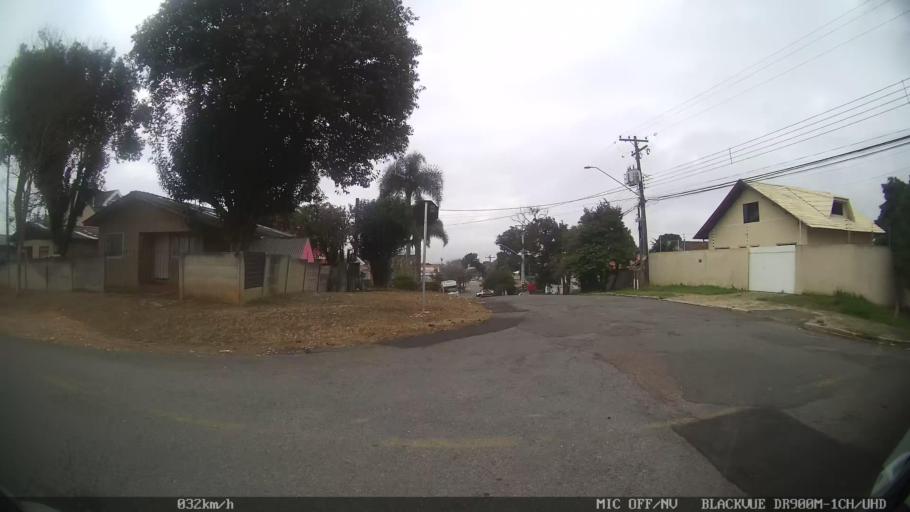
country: BR
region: Parana
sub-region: Almirante Tamandare
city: Almirante Tamandare
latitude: -25.3791
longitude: -49.3319
